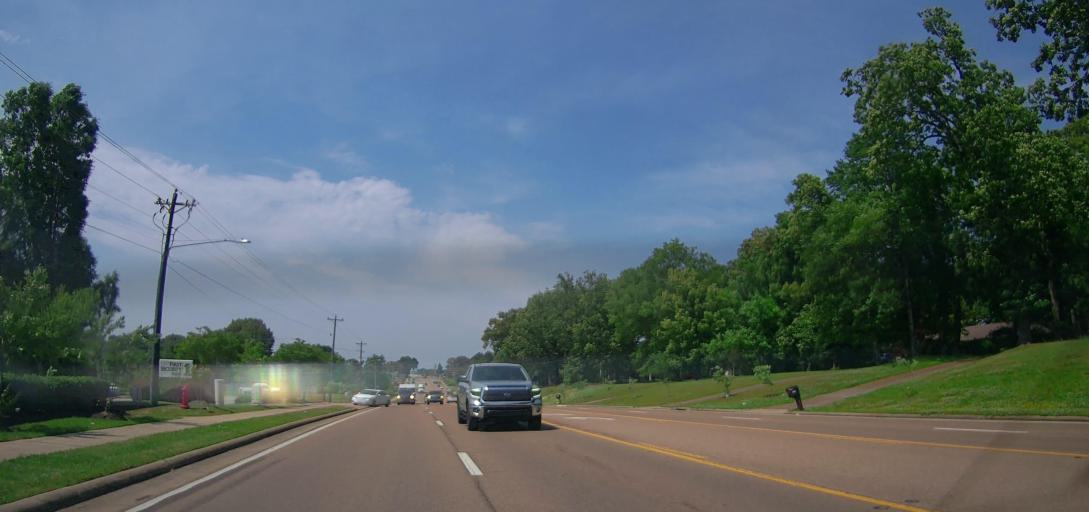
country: US
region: Mississippi
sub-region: De Soto County
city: Olive Branch
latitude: 34.9567
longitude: -89.8305
